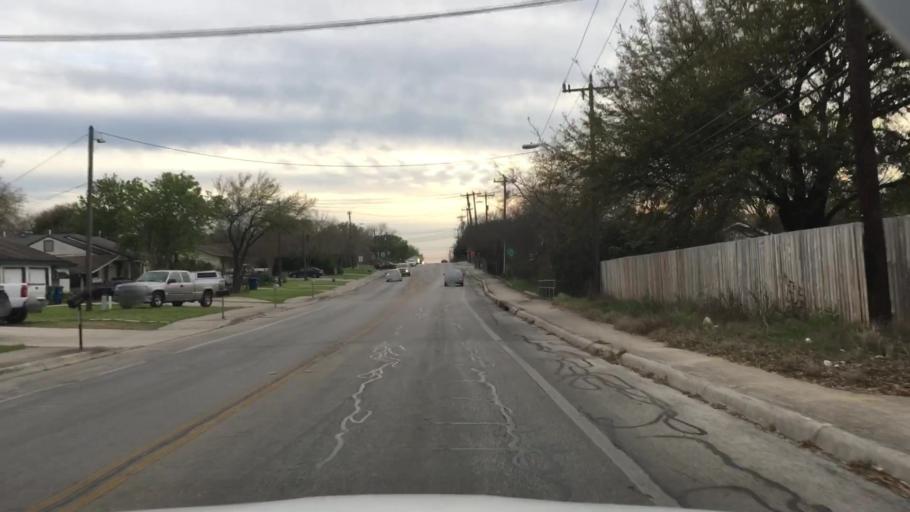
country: US
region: Texas
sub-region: Bexar County
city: Windcrest
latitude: 29.5606
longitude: -98.4013
